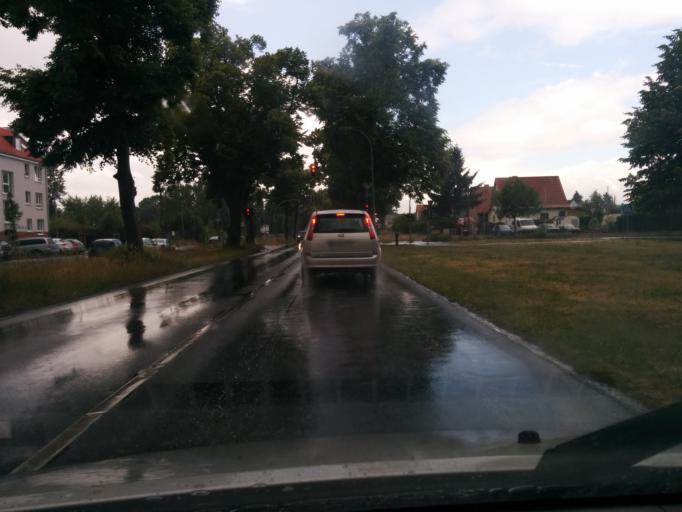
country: DE
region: Berlin
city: Staaken
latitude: 52.5590
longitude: 13.1321
